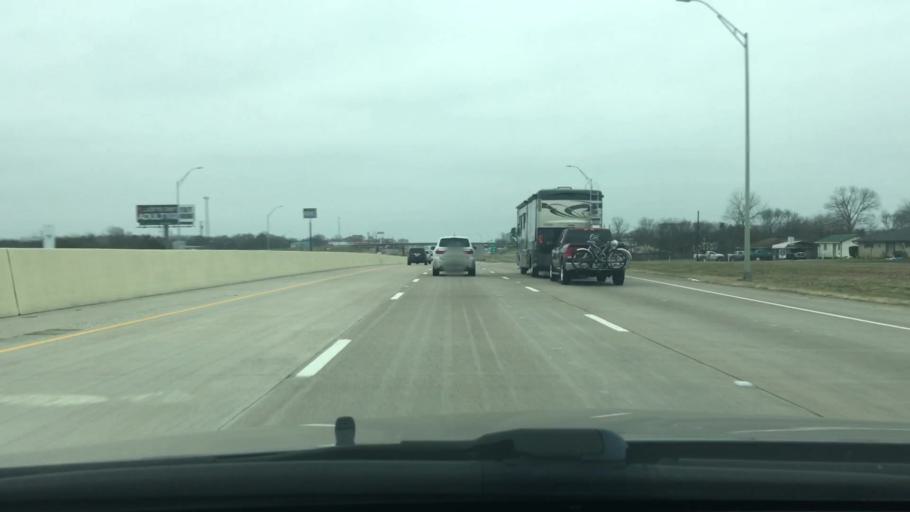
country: US
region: Texas
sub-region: Navarro County
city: Corsicana
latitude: 32.0131
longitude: -96.4360
